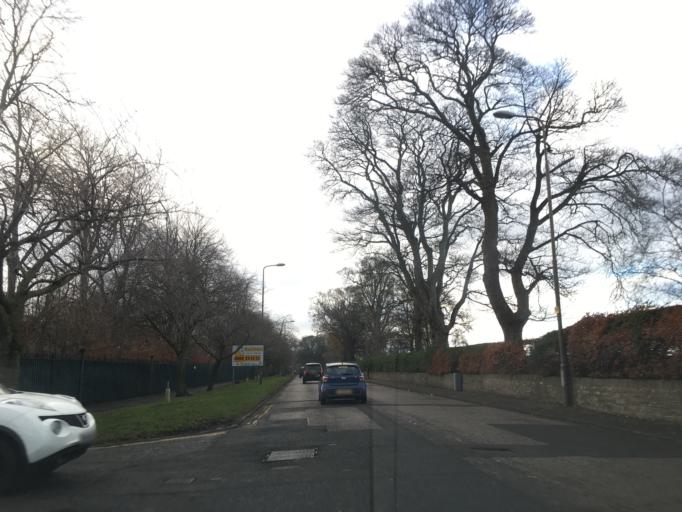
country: GB
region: Scotland
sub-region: Edinburgh
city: Colinton
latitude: 55.9129
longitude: -3.2449
